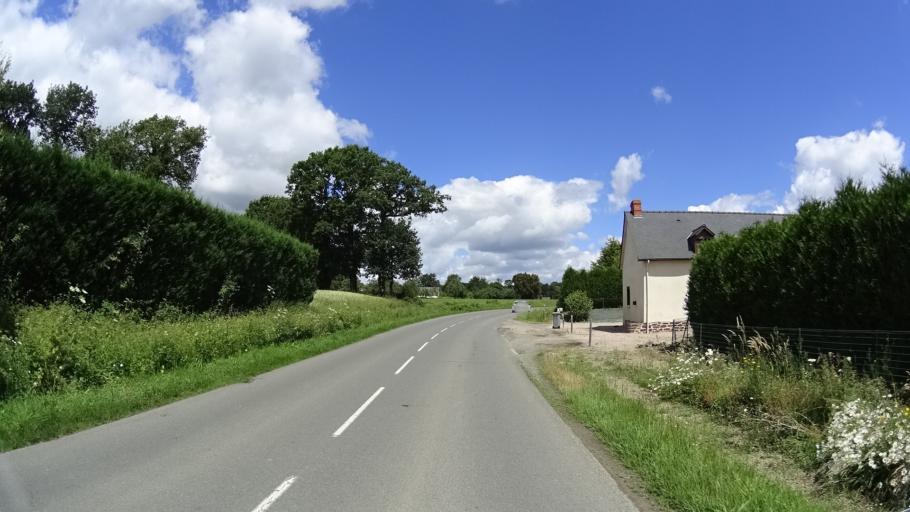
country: FR
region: Brittany
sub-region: Departement d'Ille-et-Vilaine
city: Saint-Gilles
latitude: 48.1422
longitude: -1.8286
